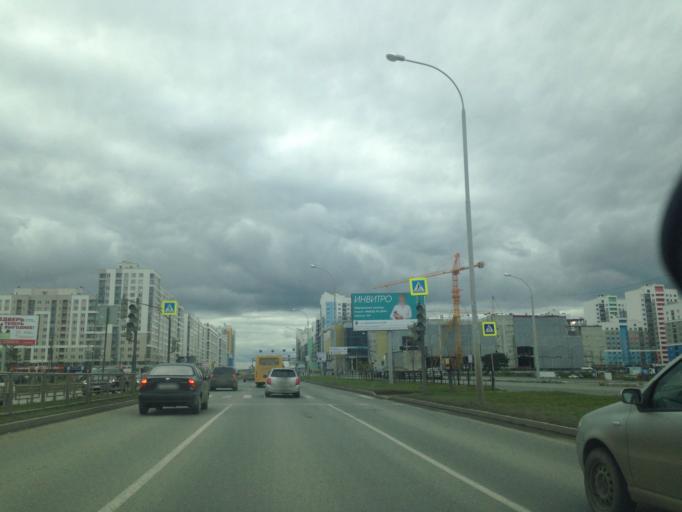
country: RU
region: Sverdlovsk
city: Shirokaya Rechka
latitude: 56.7948
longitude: 60.5245
